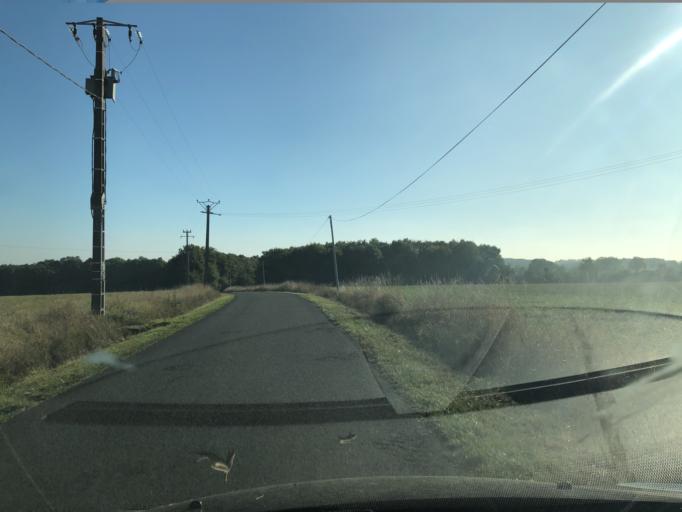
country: FR
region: Centre
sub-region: Departement d'Indre-et-Loire
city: Neuvy-le-Roi
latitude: 47.6598
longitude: 0.6087
